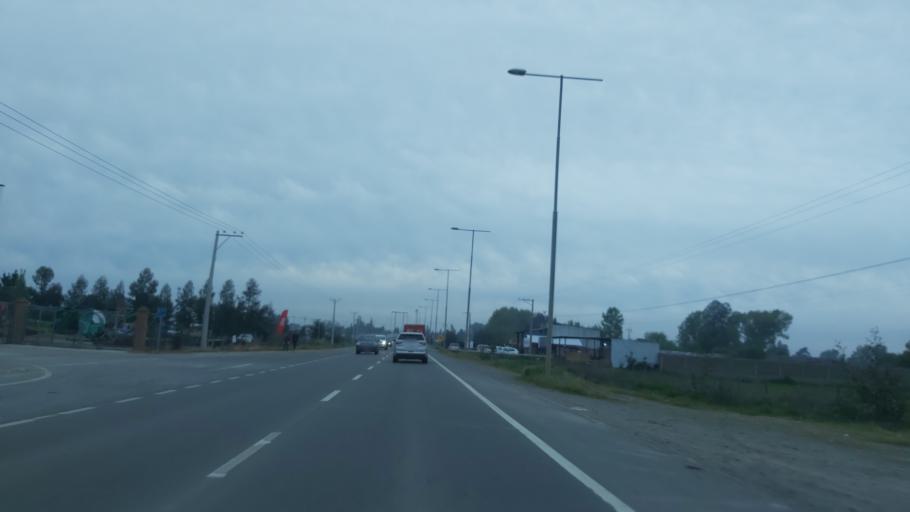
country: CL
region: Maule
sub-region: Provincia de Linares
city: Linares
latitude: -35.8357
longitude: -71.6218
